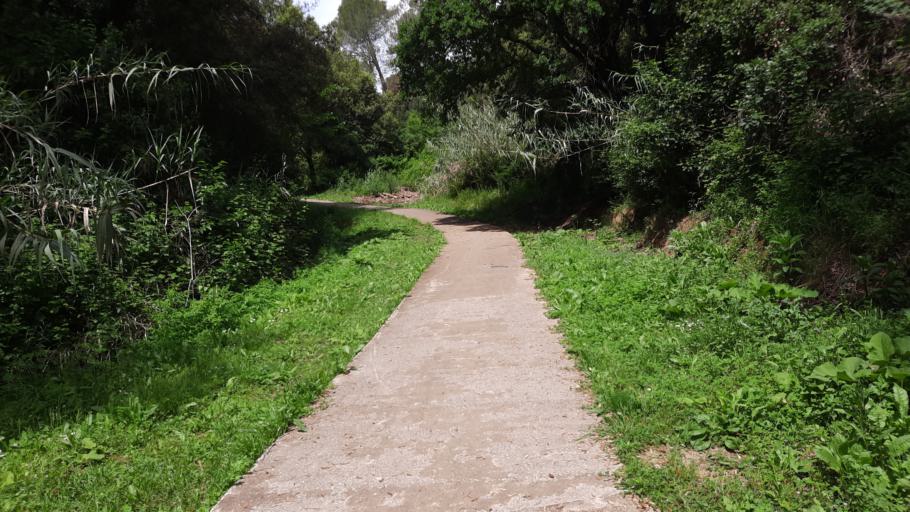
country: ES
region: Catalonia
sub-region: Provincia de Barcelona
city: Sant Quirze del Valles
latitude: 41.5025
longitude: 2.0833
